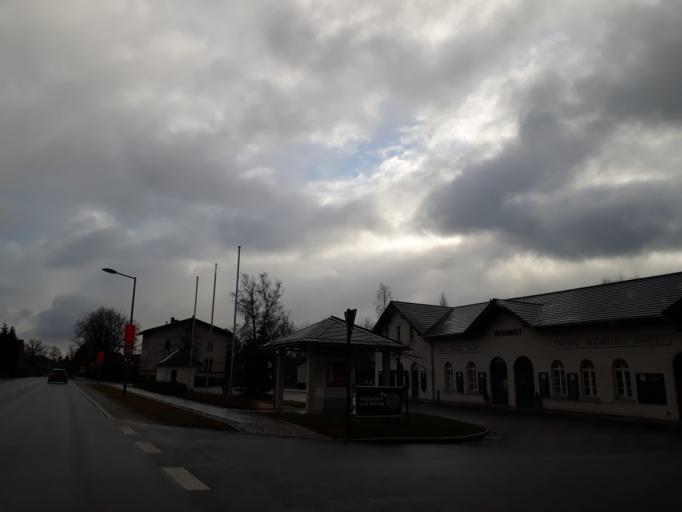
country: DE
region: Saxony
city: Herrnhut
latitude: 51.0210
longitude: 14.7364
